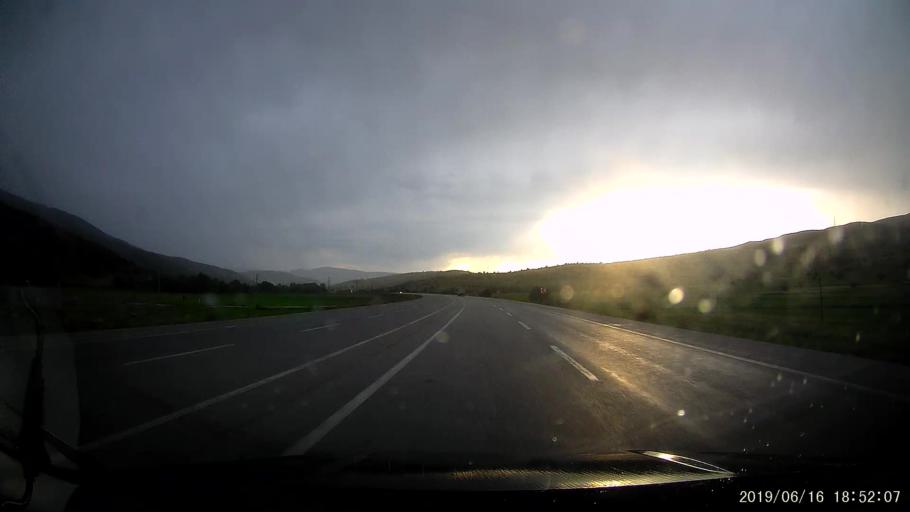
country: TR
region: Erzincan
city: Catalcam
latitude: 39.9030
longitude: 38.9101
